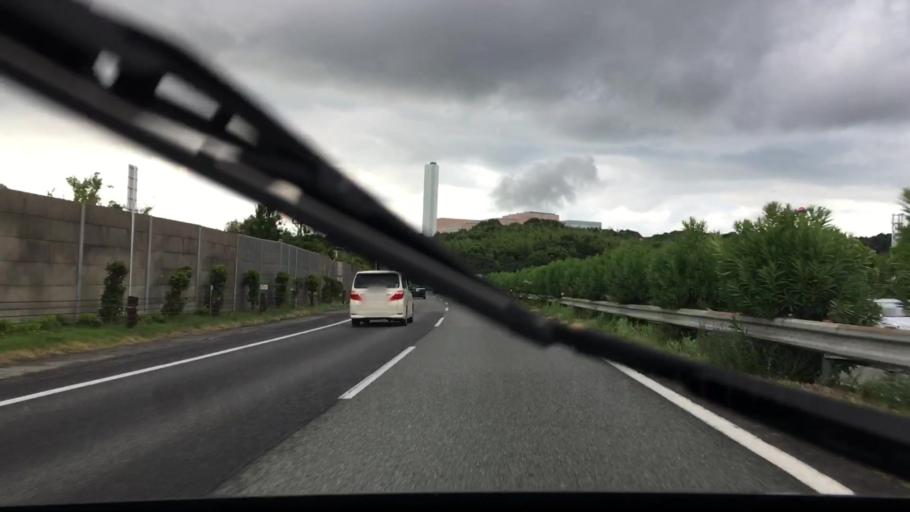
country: JP
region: Fukuoka
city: Sasaguri
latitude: 33.6375
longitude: 130.4901
